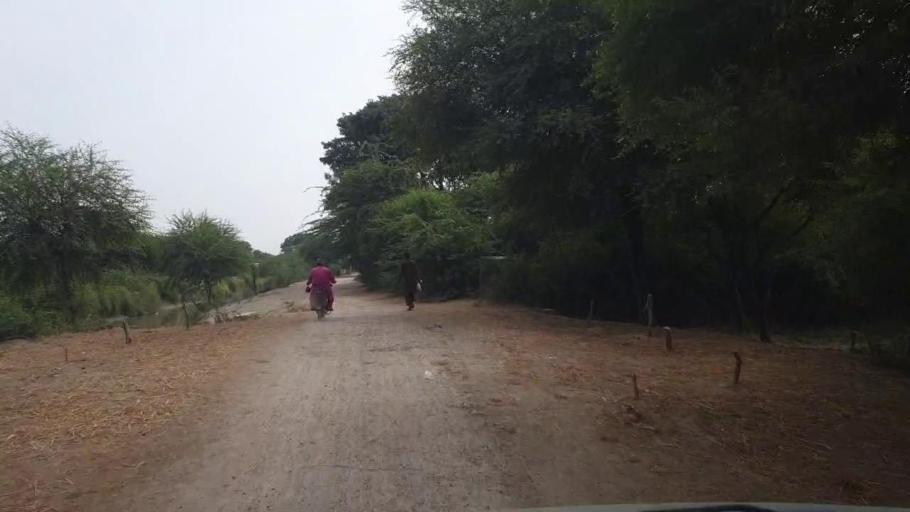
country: PK
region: Sindh
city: Matli
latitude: 24.9833
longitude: 68.7028
